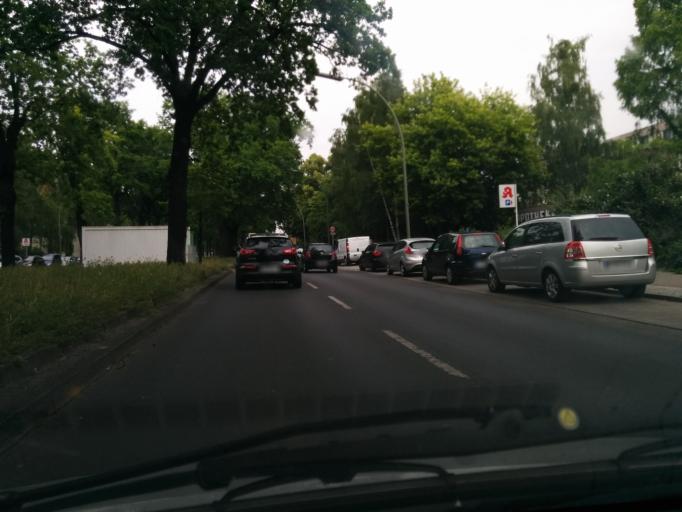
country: DE
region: Berlin
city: Dahlem
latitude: 52.4403
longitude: 13.2782
